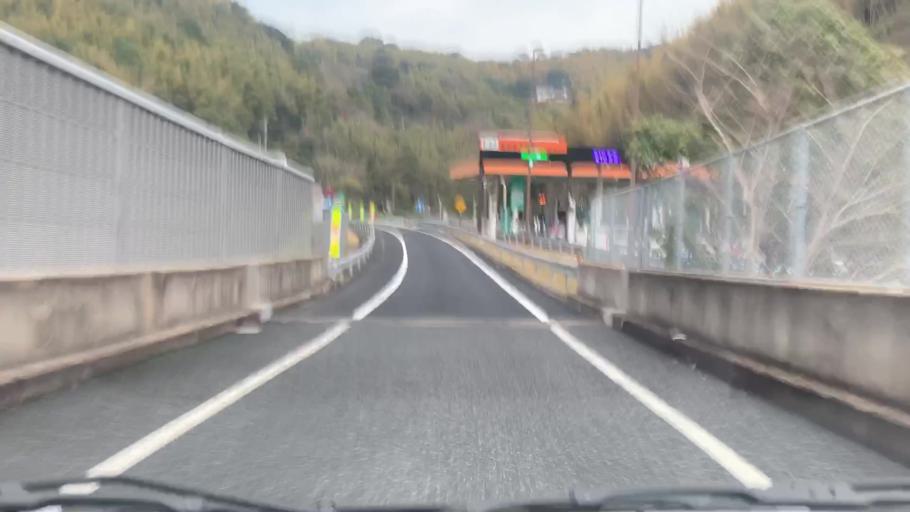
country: JP
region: Nagasaki
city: Nagasaki-shi
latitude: 32.7282
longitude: 129.9031
